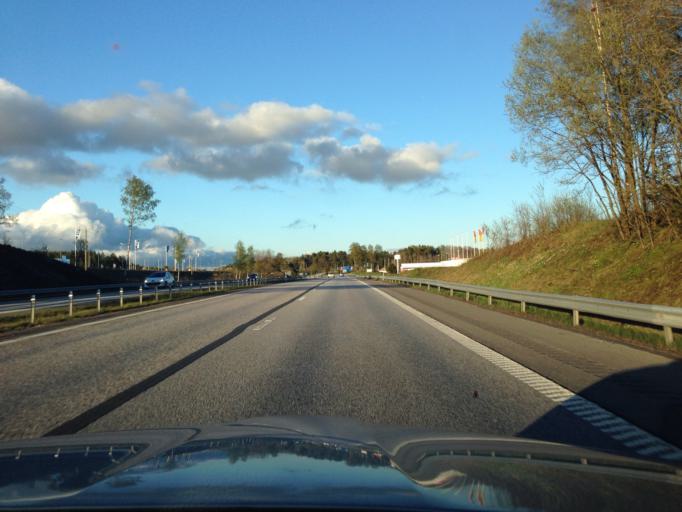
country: SE
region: Soedermanland
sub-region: Nykopings Kommun
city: Nykoping
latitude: 58.7703
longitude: 17.0142
